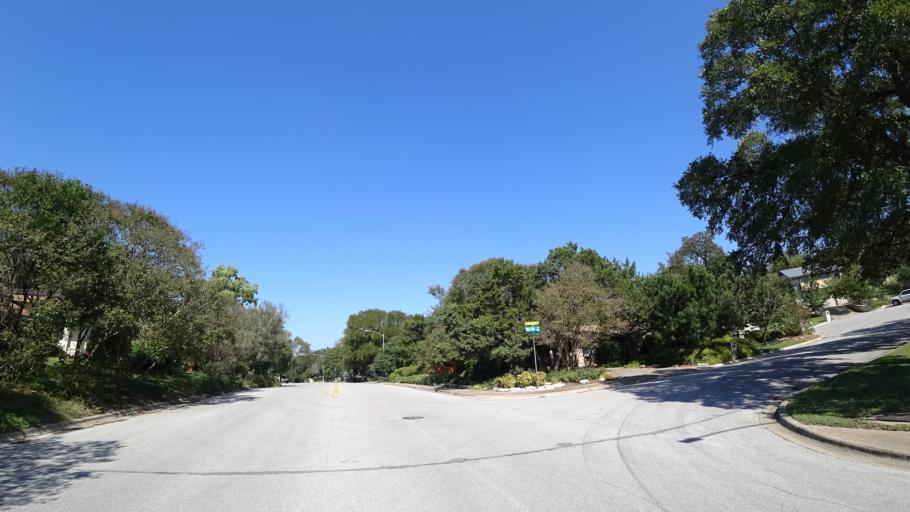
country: US
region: Texas
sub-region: Travis County
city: Rollingwood
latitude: 30.2510
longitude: -97.7928
